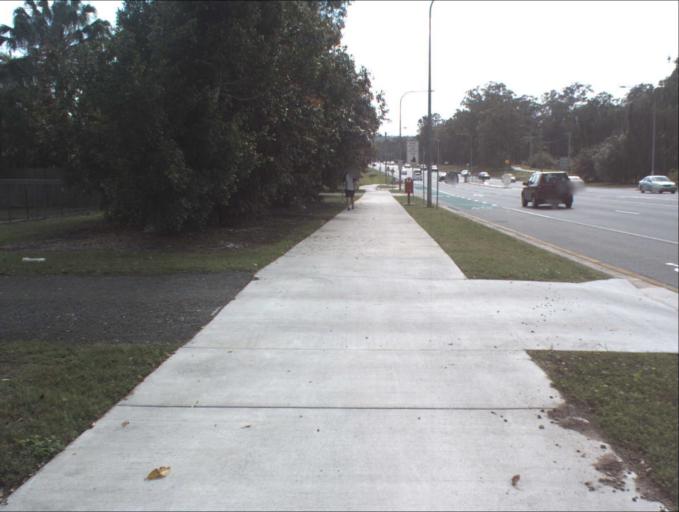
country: AU
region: Queensland
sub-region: Logan
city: Woodridge
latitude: -27.6570
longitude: 153.0646
